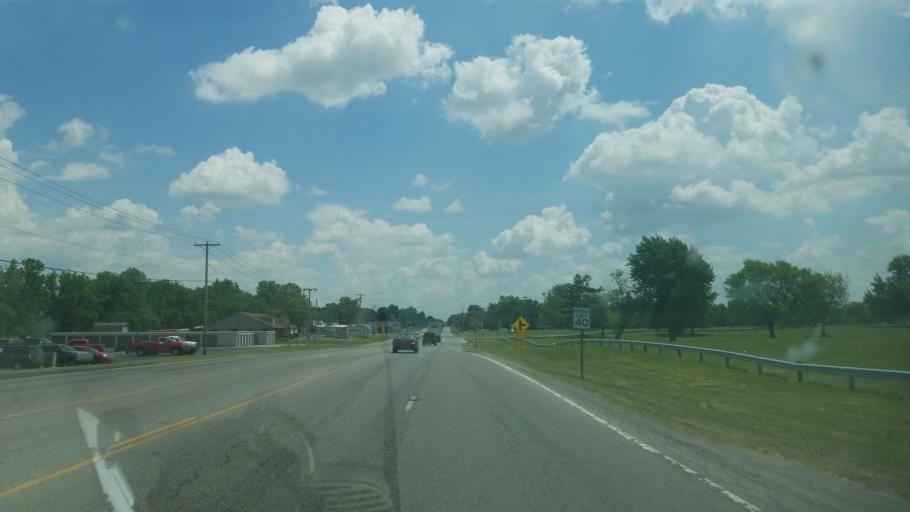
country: US
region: Ohio
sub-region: Allen County
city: Lima
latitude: 40.7308
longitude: -84.0541
